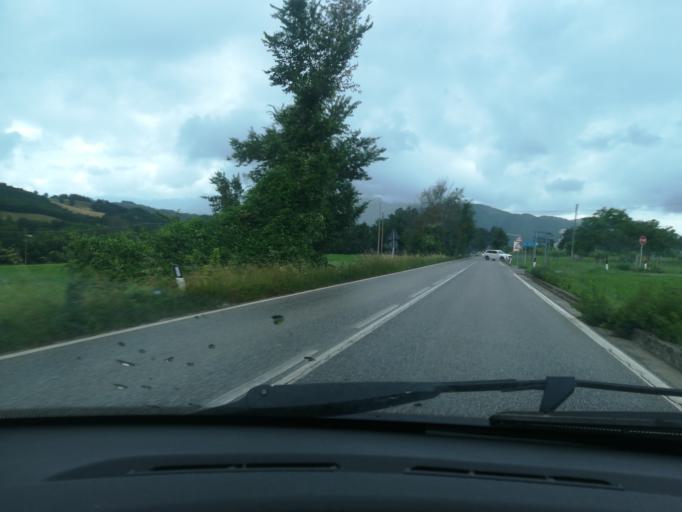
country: IT
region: The Marches
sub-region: Provincia di Macerata
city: San Ginesio
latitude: 43.0843
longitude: 13.2989
